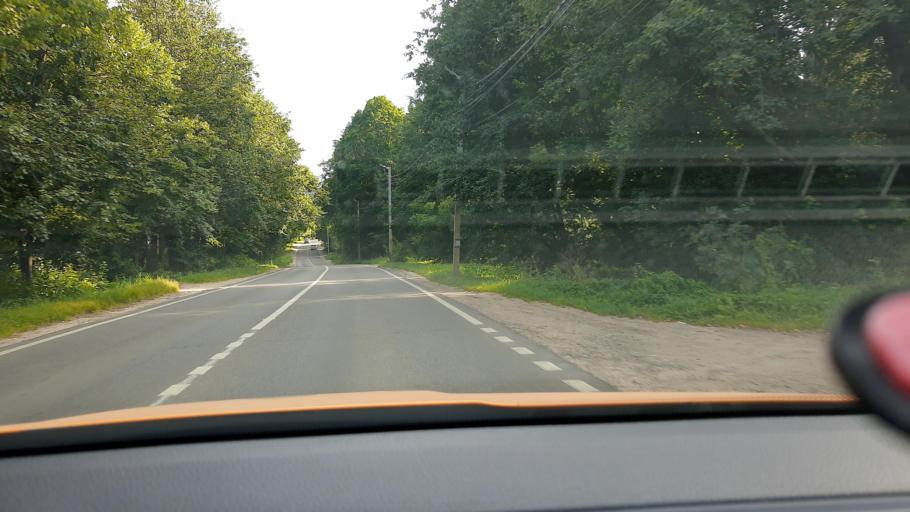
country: RU
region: Moskovskaya
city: Zvenigorod
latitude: 55.7398
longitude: 36.8492
